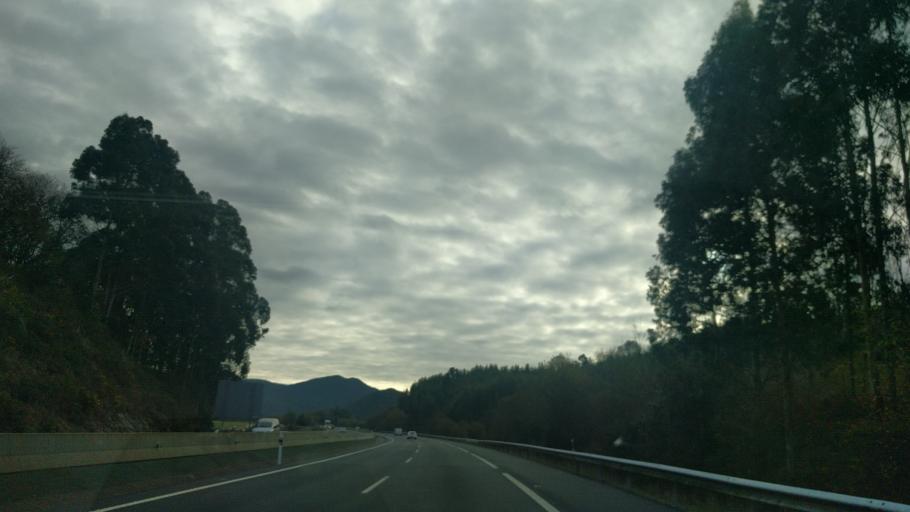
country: ES
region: Cantabria
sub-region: Provincia de Cantabria
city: Liendo
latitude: 43.3897
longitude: -3.3924
